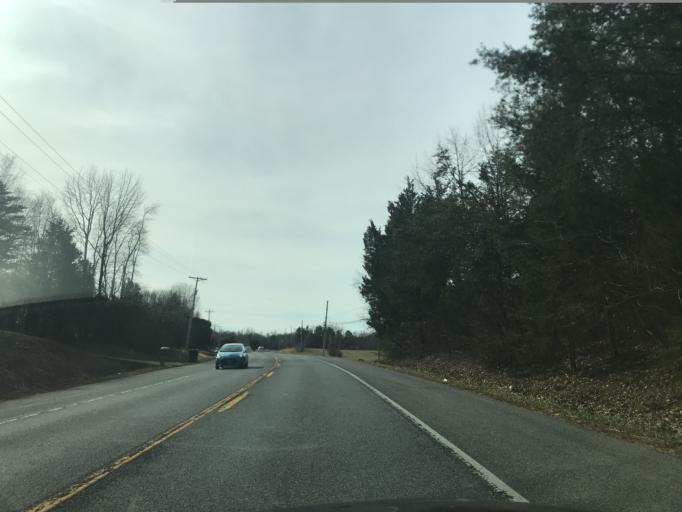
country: US
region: Maryland
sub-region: Charles County
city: La Plata
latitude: 38.4971
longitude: -77.0651
